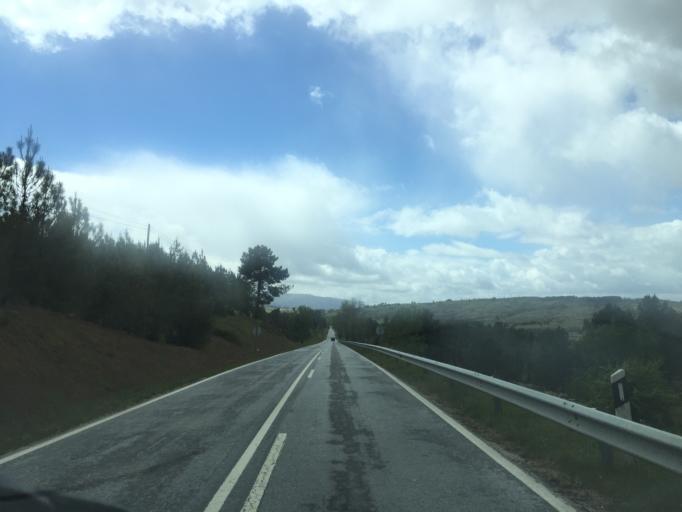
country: PT
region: Guarda
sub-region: Celorico da Beira
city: Celorico da Beira
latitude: 40.5803
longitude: -7.4539
